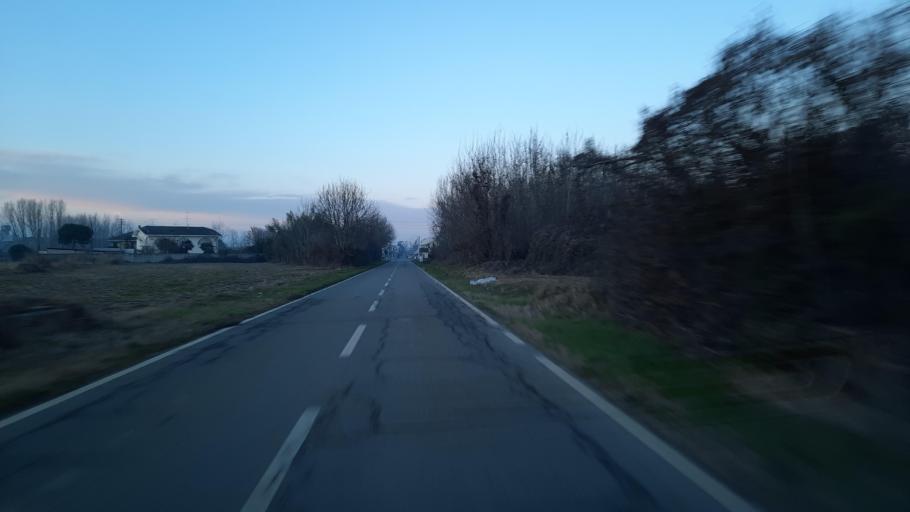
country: IT
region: Piedmont
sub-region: Provincia di Vercelli
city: Trino
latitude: 45.1823
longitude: 8.2957
